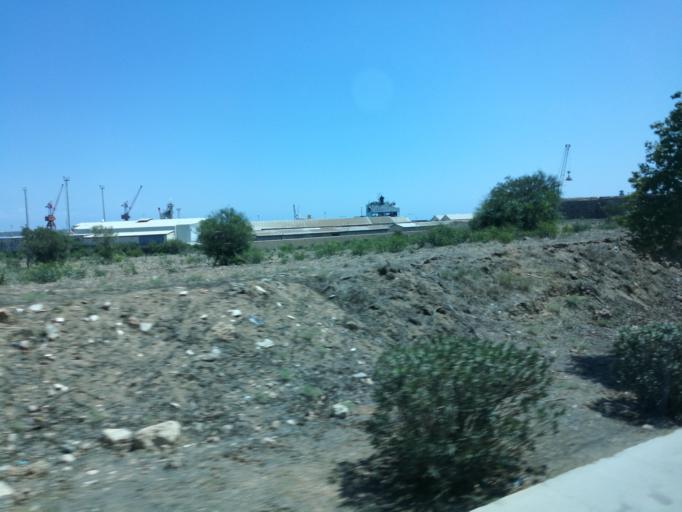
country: CY
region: Ammochostos
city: Famagusta
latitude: 35.1293
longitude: 33.9380
